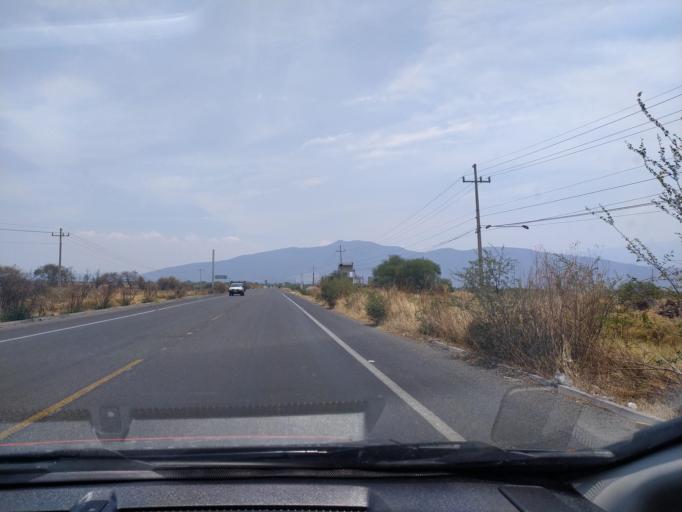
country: MX
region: Jalisco
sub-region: Zacoalco de Torres
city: Barranca de Otates (Barranca de Otatan)
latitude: 20.3101
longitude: -103.5936
